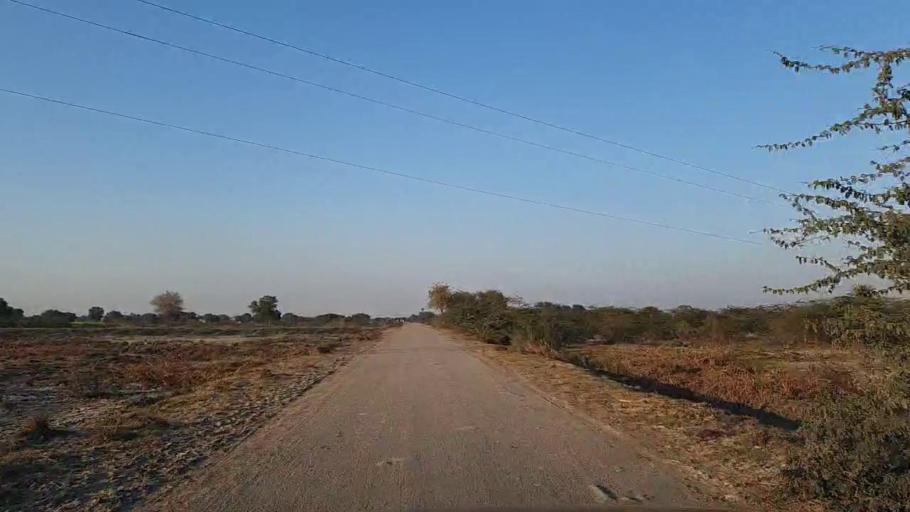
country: PK
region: Sindh
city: Nawabshah
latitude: 26.2214
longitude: 68.3379
